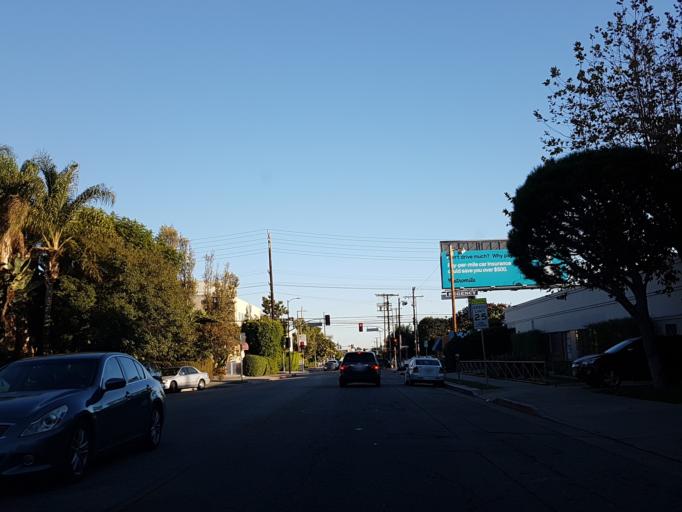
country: US
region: California
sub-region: Los Angeles County
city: Westwood, Los Angeles
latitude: 34.0364
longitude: -118.4497
